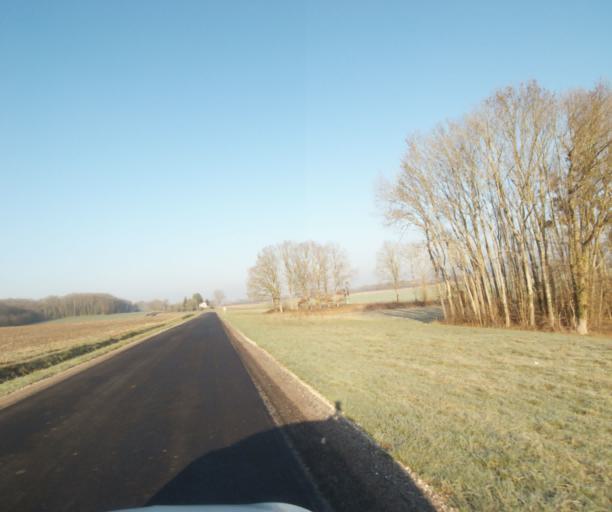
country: FR
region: Champagne-Ardenne
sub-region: Departement de la Haute-Marne
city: Montier-en-Der
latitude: 48.4848
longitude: 4.7439
